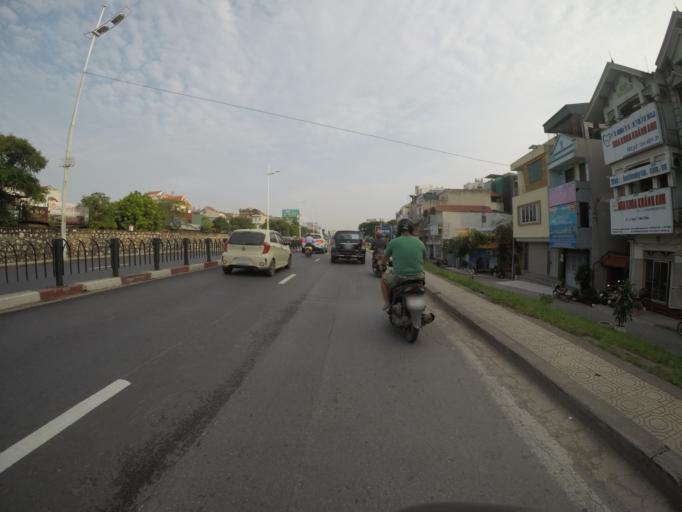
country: VN
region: Ha Noi
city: Tay Ho
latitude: 21.0794
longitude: 105.8192
